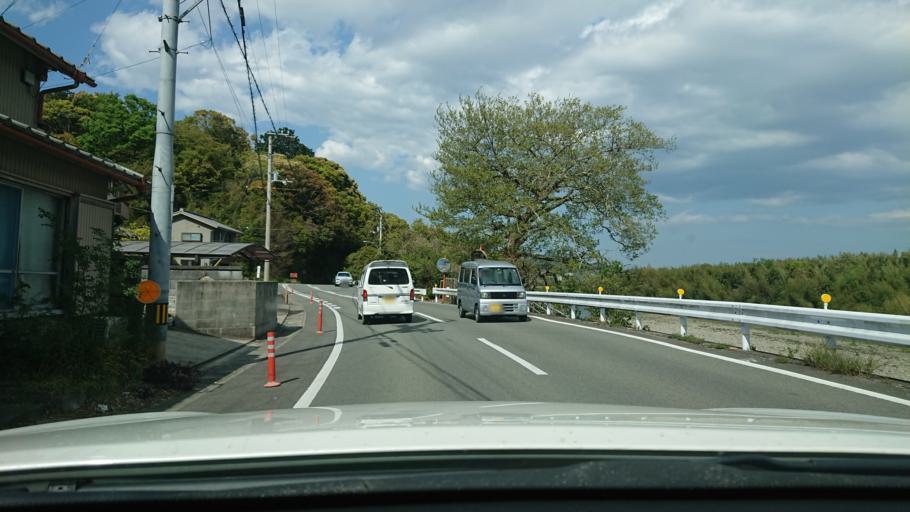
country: JP
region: Tokushima
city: Komatsushimacho
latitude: 34.0031
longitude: 134.5495
